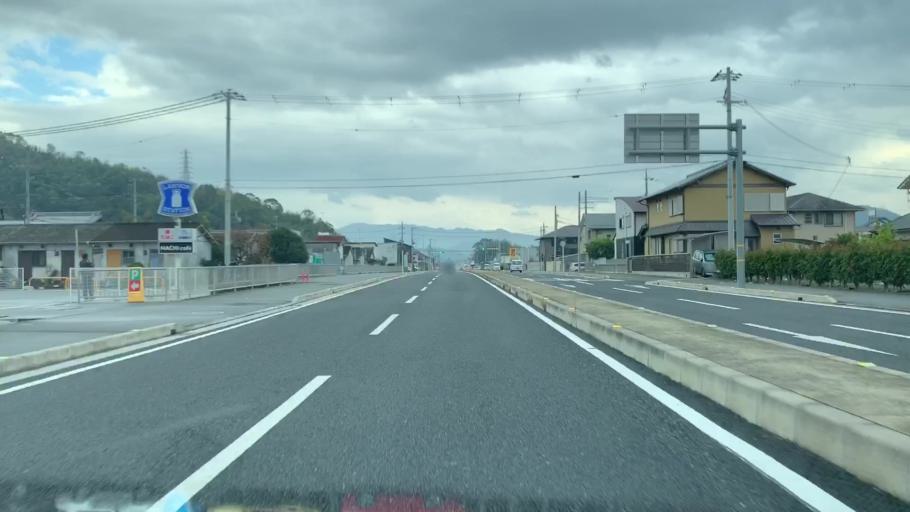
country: JP
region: Wakayama
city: Wakayama-shi
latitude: 34.2162
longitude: 135.2076
